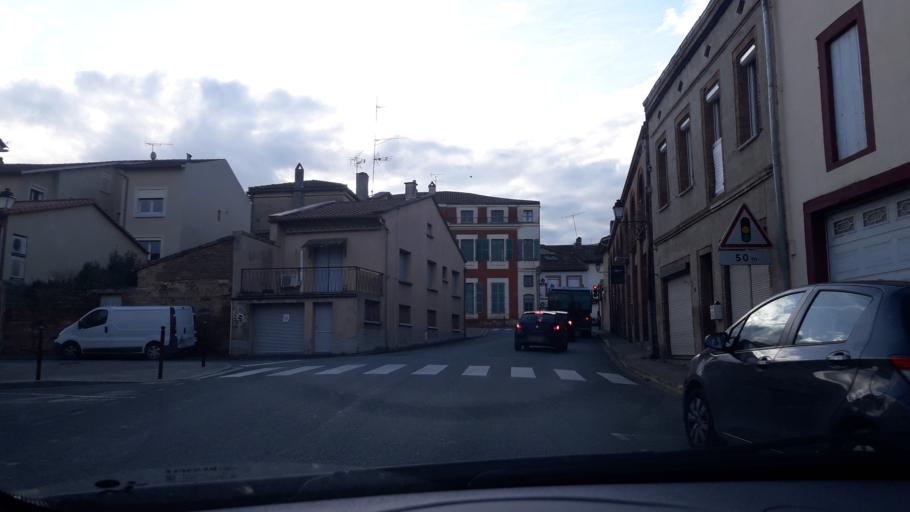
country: FR
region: Midi-Pyrenees
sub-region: Departement de la Haute-Garonne
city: Levignac
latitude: 43.6666
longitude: 1.1931
